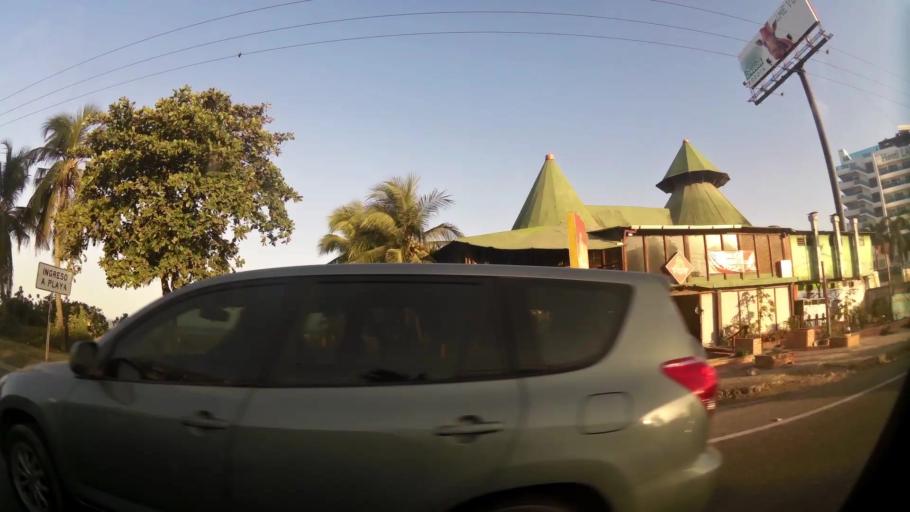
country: CO
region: Bolivar
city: Cartagena
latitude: 10.4582
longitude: -75.5085
